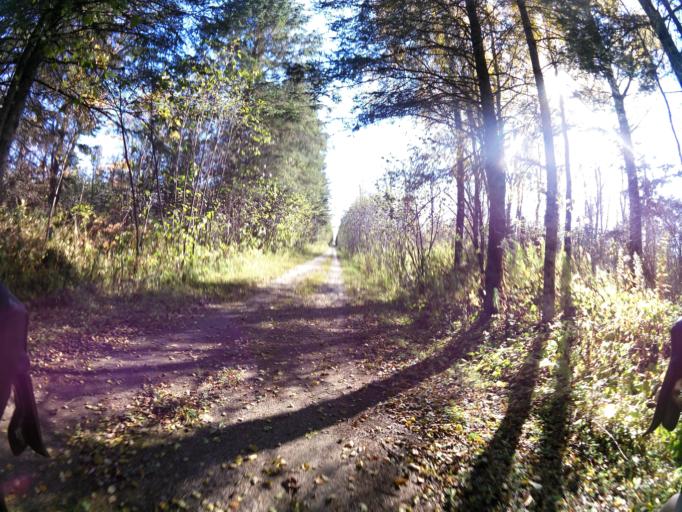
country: CA
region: Quebec
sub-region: Outaouais
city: Wakefield
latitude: 45.8889
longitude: -76.0330
